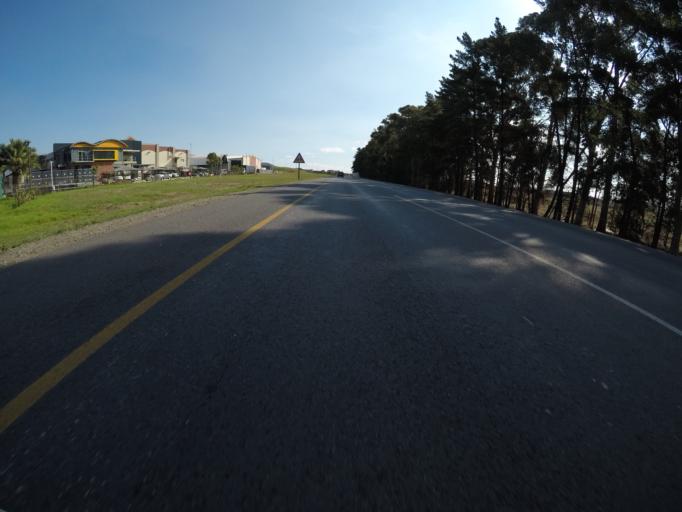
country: ZA
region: Western Cape
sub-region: Cape Winelands District Municipality
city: Stellenbosch
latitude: -33.8764
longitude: 18.8093
